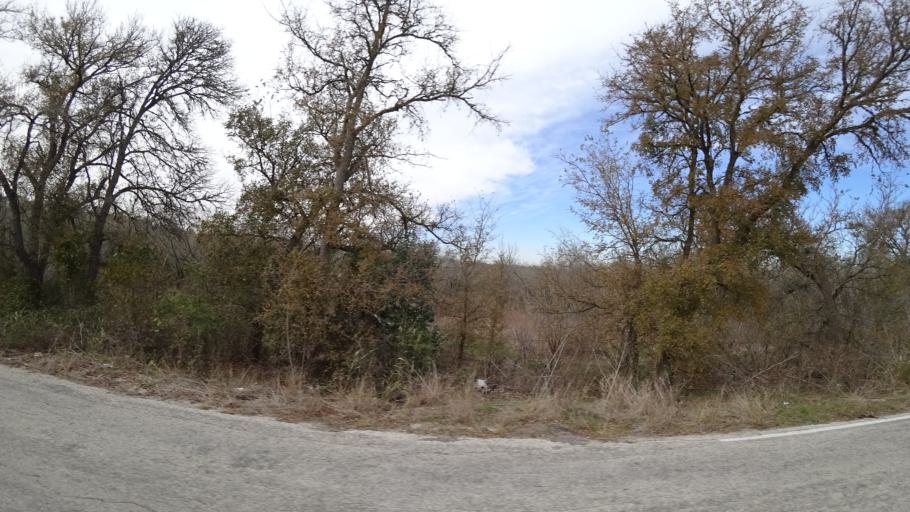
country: US
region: Texas
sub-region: Travis County
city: Garfield
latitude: 30.1427
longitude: -97.5663
